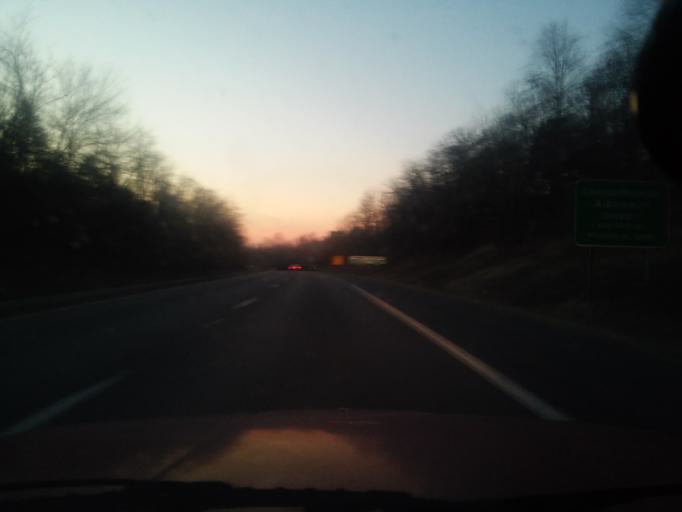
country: US
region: Virginia
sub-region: City of Charlottesville
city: Charlottesville
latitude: 38.0213
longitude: -78.4190
